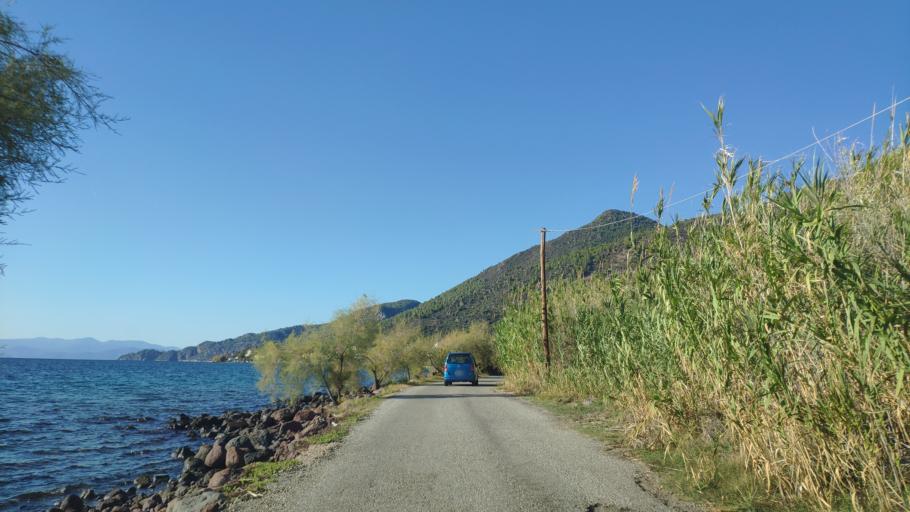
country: GR
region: Attica
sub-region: Nomos Piraios
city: Megalochori
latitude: 37.5849
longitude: 23.3487
